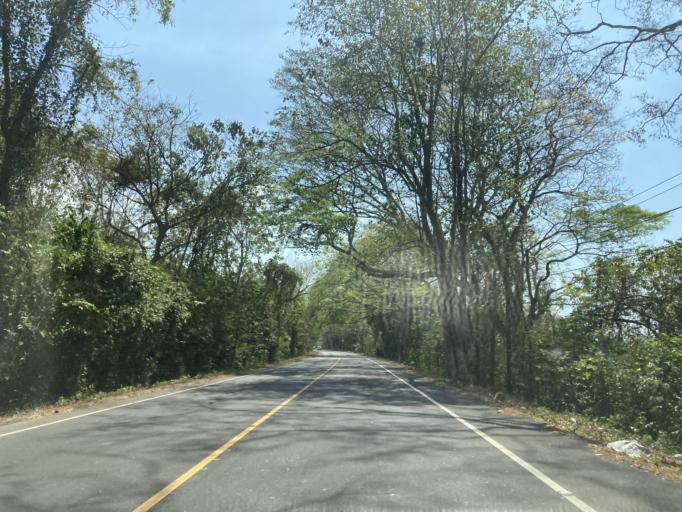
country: GT
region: Escuintla
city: Guanagazapa
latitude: 14.1803
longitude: -90.6883
